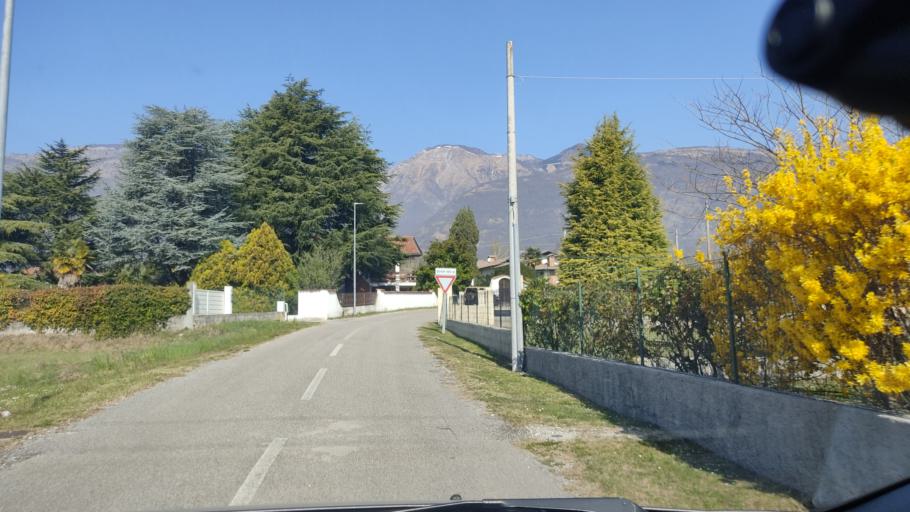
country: IT
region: Friuli Venezia Giulia
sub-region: Provincia di Pordenone
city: Budoia
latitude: 46.0500
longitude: 12.5412
